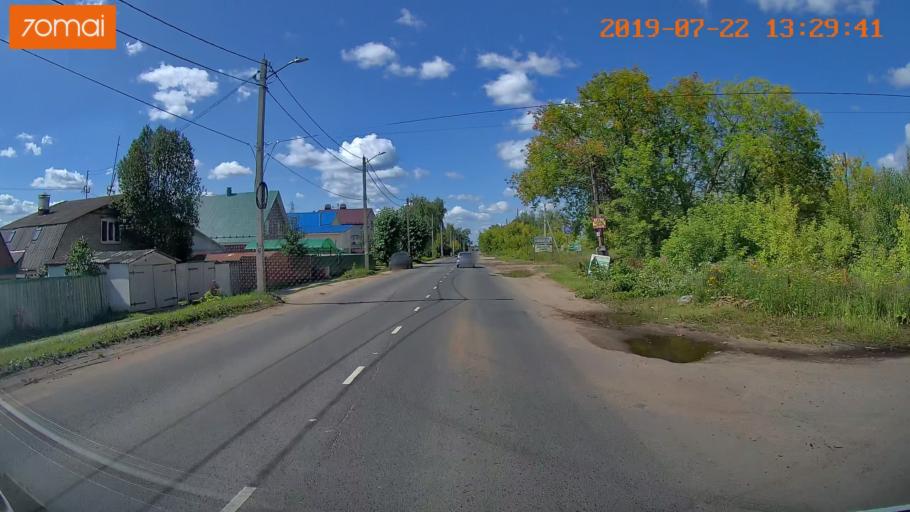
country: RU
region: Ivanovo
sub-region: Gorod Ivanovo
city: Ivanovo
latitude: 57.0487
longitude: 40.9354
